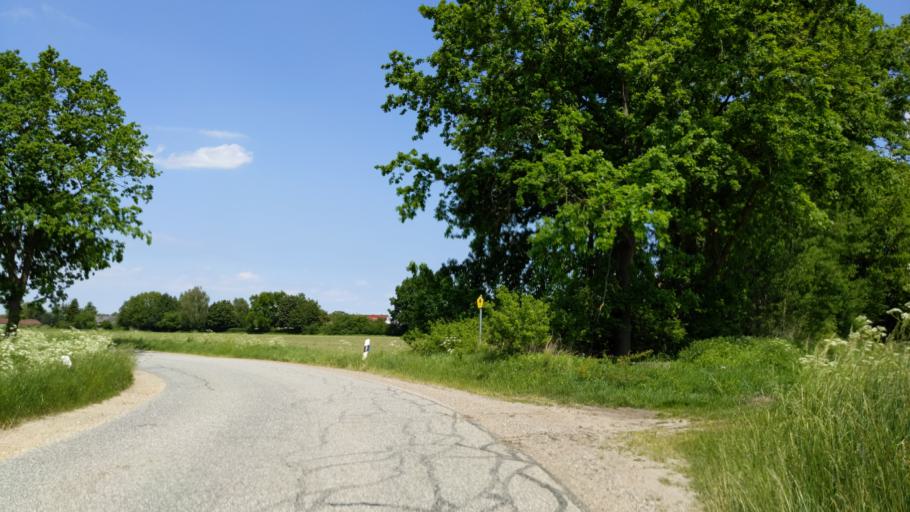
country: DE
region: Schleswig-Holstein
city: Krummesse
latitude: 53.8265
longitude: 10.6624
